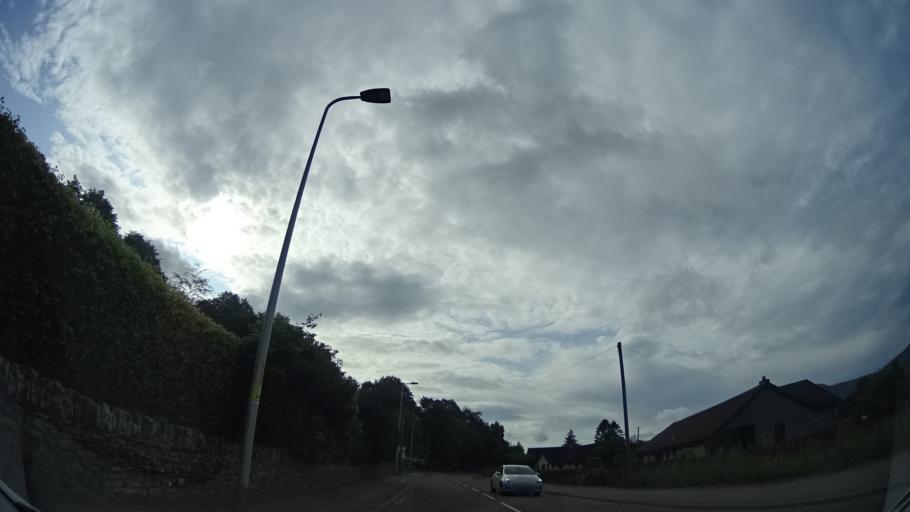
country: GB
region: Scotland
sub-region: Highland
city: Muir of Ord
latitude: 57.5692
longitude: -4.5805
